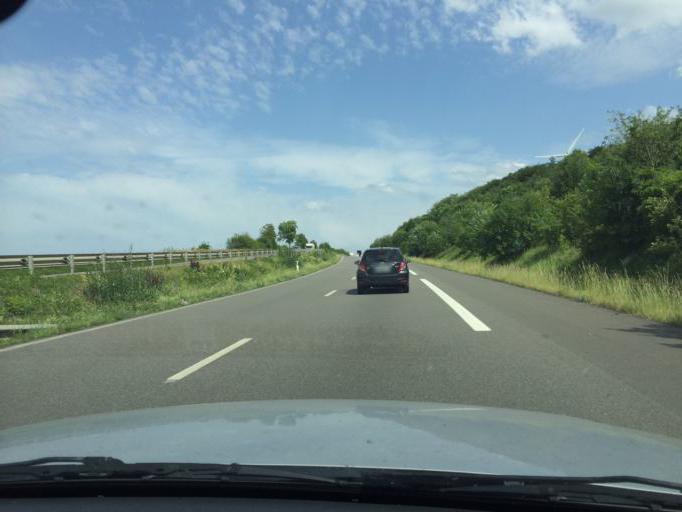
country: FR
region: Lorraine
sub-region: Departement de la Meuse
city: Lerouville
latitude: 48.7054
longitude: 5.4995
